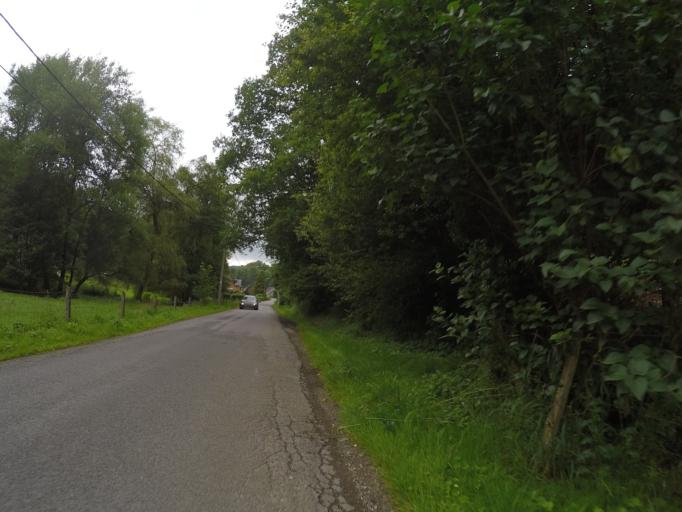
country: BE
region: Wallonia
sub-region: Province de Namur
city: Yvoir
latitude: 50.3465
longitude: 4.9511
